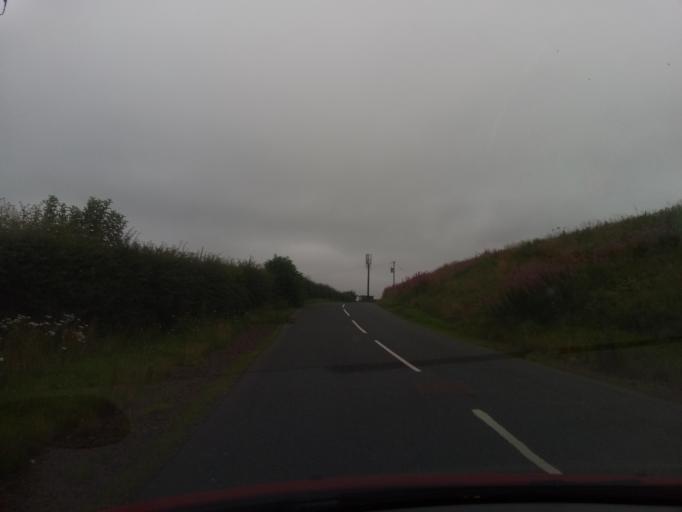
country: GB
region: Scotland
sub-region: Fife
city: Pathhead
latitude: 55.7756
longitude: -2.9522
